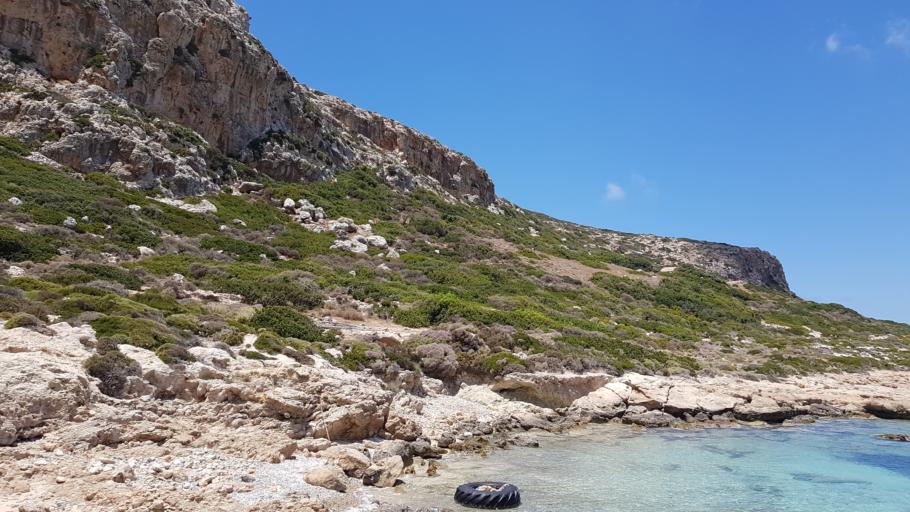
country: GR
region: Crete
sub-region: Nomos Chanias
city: Kissamos
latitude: 35.5855
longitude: 23.5865
